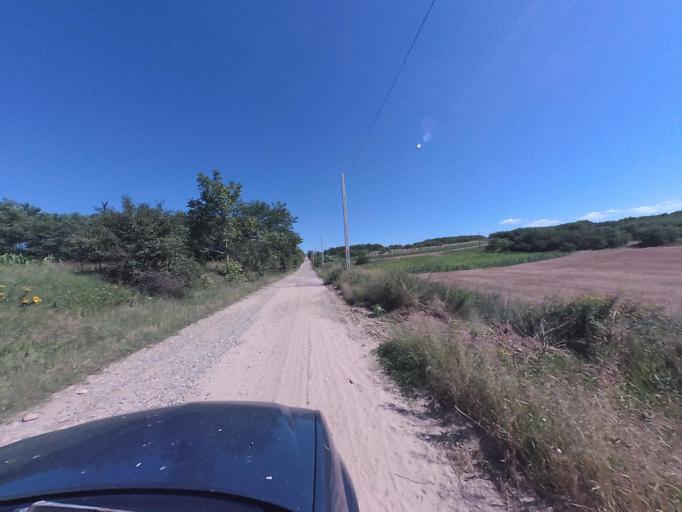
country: RO
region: Vaslui
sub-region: Comuna Costesti
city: Costesti
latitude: 46.4820
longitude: 27.7691
